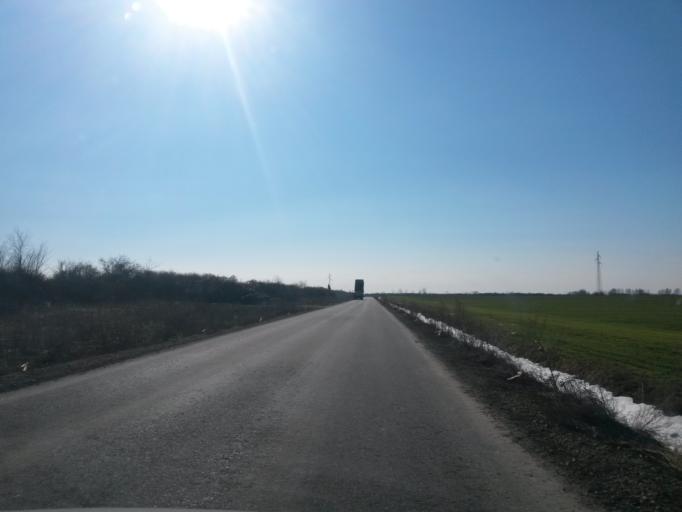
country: HR
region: Vukovarsko-Srijemska
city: Vukovar
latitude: 45.3154
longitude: 19.0023
